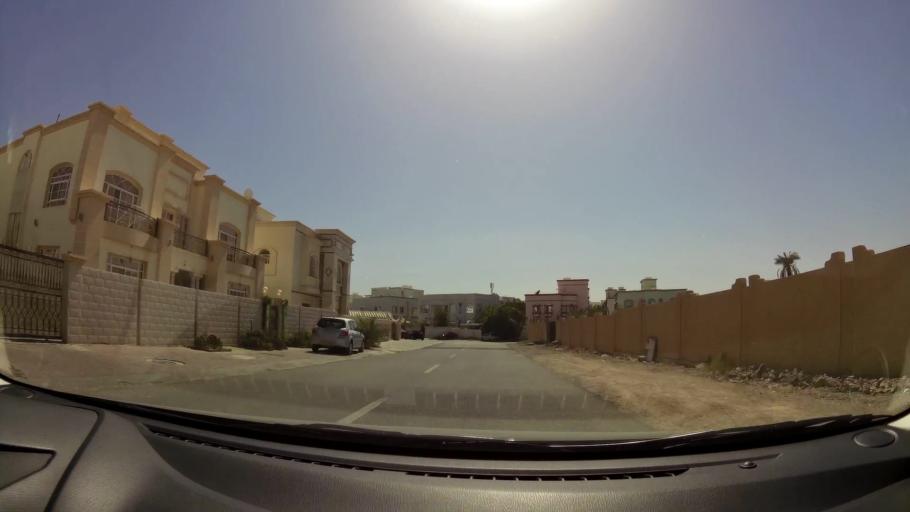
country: OM
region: Muhafazat Masqat
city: As Sib al Jadidah
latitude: 23.6096
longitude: 58.2376
